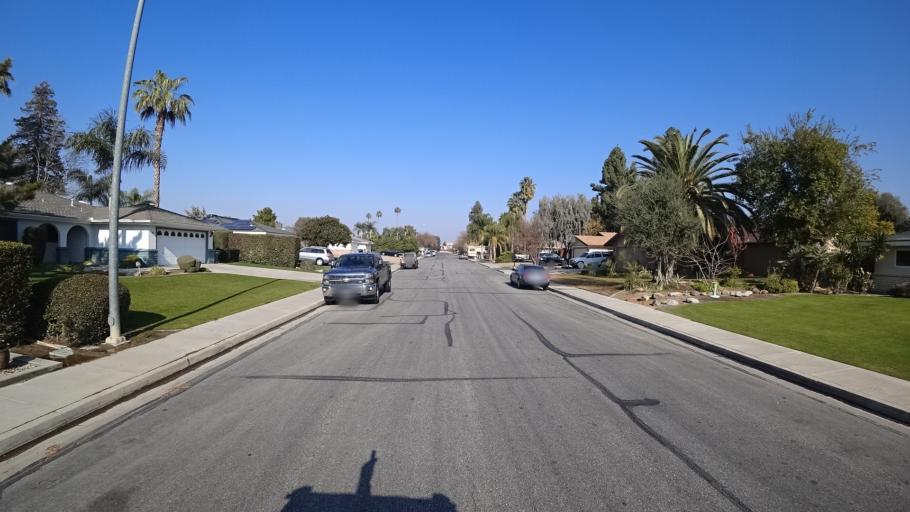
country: US
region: California
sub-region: Kern County
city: Greenacres
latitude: 35.3574
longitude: -119.0749
